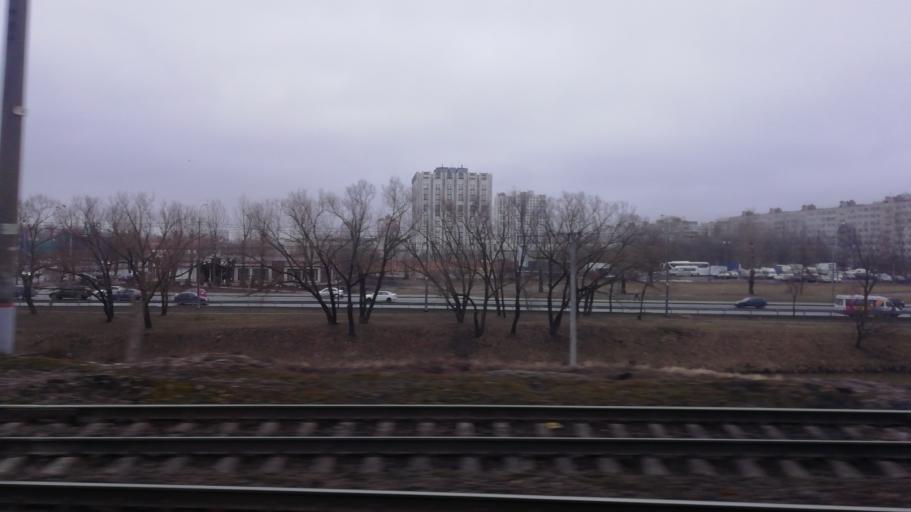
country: RU
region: St.-Petersburg
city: Kupchino
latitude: 59.8730
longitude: 30.3549
